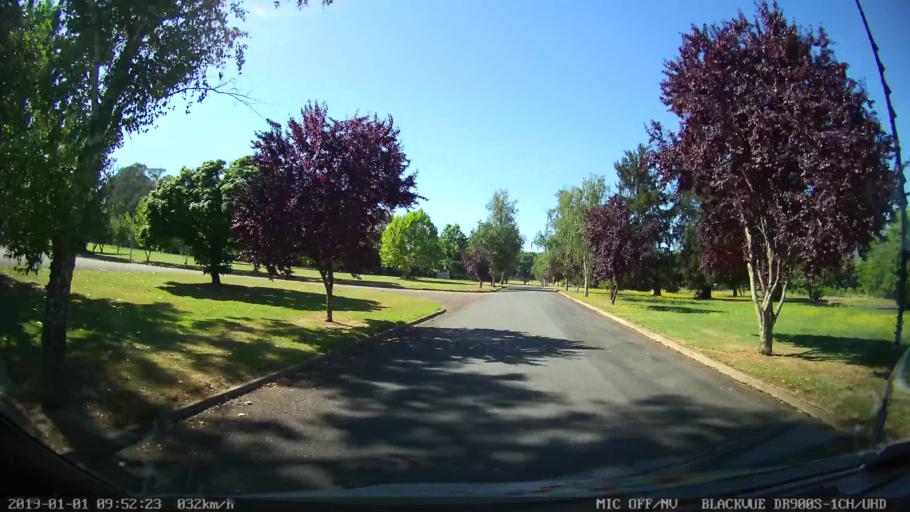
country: AU
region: New South Wales
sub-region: Snowy River
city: Jindabyne
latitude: -36.2178
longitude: 148.1242
